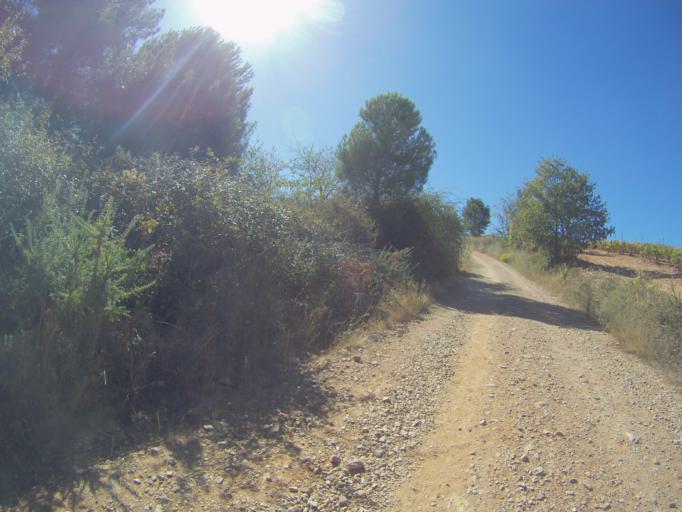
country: ES
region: Castille and Leon
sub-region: Provincia de Leon
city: Villafranca del Bierzo
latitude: 42.6095
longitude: -6.7774
